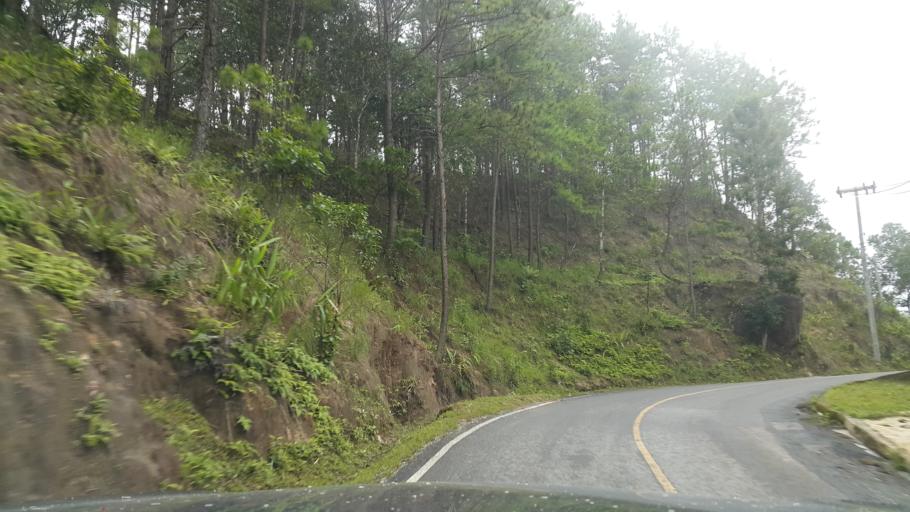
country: TH
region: Chiang Mai
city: Samoeng
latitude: 18.8816
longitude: 98.5242
